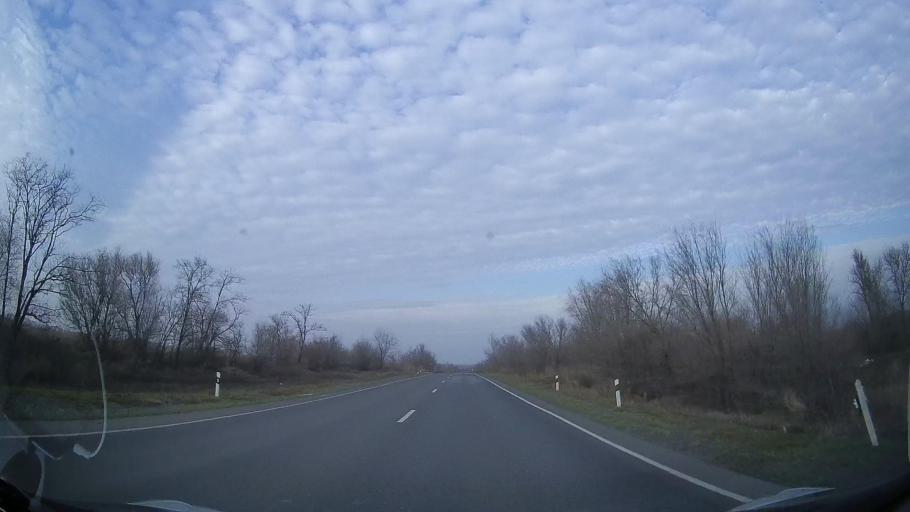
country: RU
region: Rostov
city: Bagayevskaya
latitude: 47.1573
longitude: 40.2764
